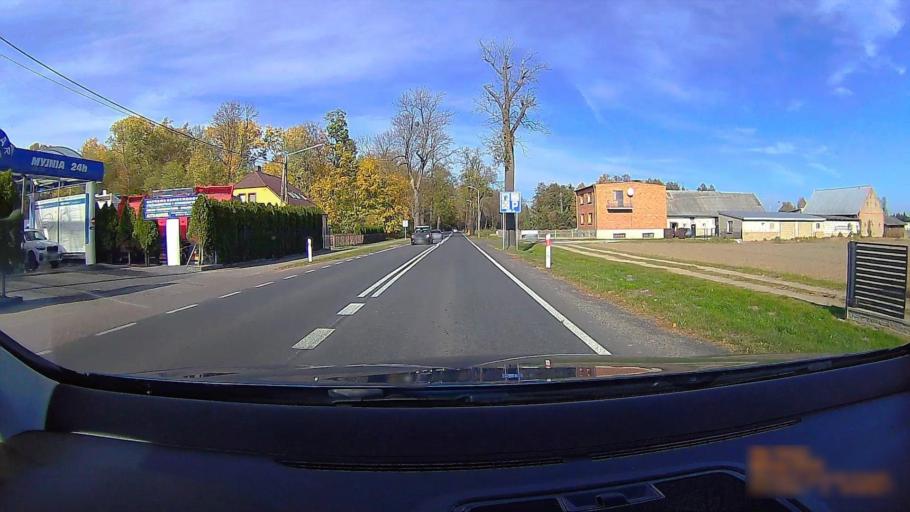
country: PL
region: Greater Poland Voivodeship
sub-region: Powiat ostrzeszowski
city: Doruchow
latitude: 51.4126
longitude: 18.0763
